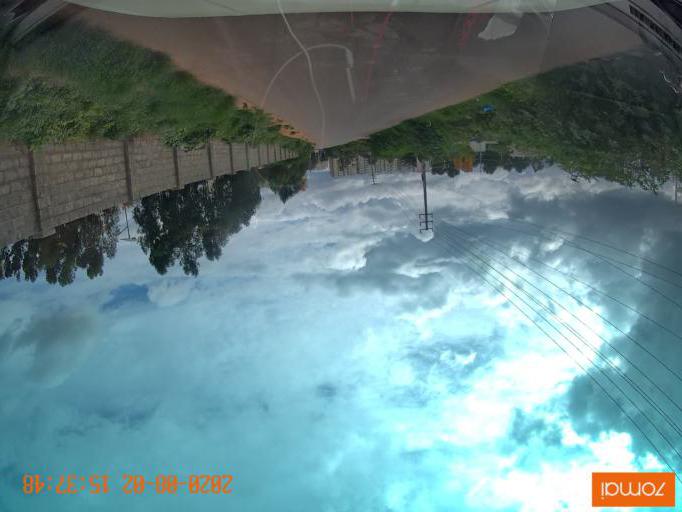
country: IN
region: Karnataka
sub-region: Bangalore Urban
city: Anekal
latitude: 12.8360
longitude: 77.6459
